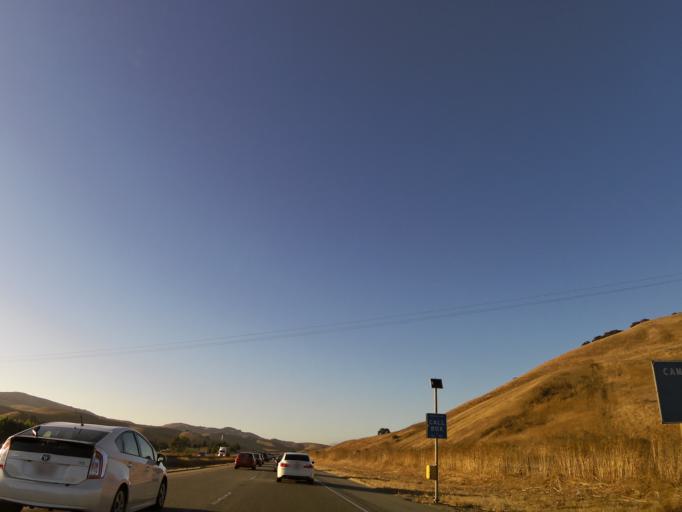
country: US
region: California
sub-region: San Benito County
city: San Juan Bautista
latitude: 36.8947
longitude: -121.5563
